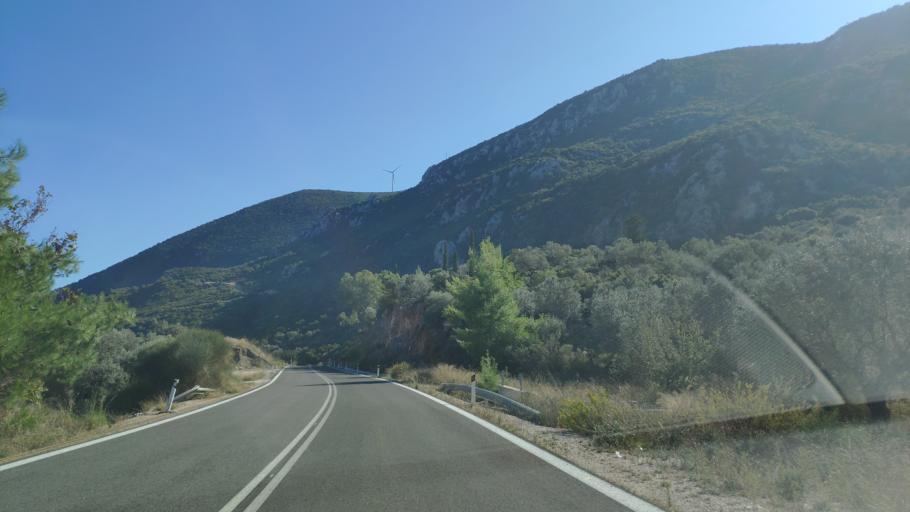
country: GR
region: Peloponnese
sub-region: Nomos Argolidos
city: Didyma
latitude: 37.5589
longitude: 23.2577
